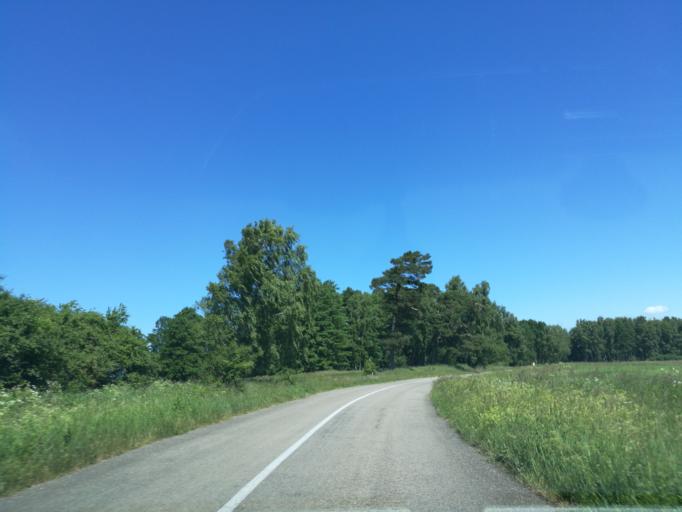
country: LT
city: Neringa
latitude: 55.3767
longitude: 21.2239
